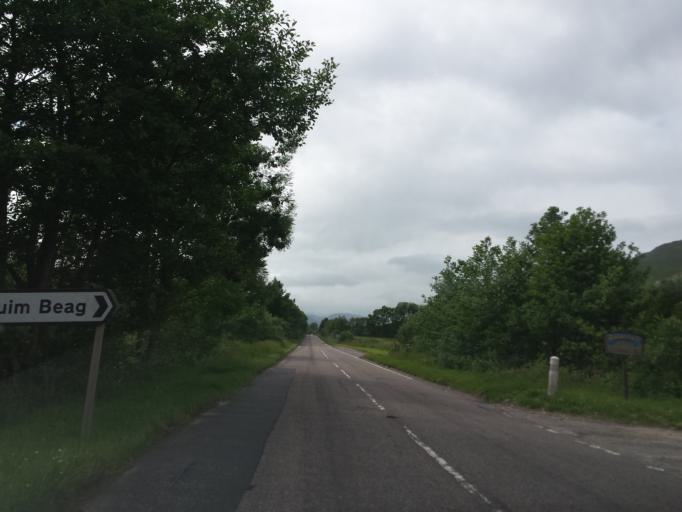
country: GB
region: Scotland
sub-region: Highland
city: Fort William
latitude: 56.8552
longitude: -5.2708
